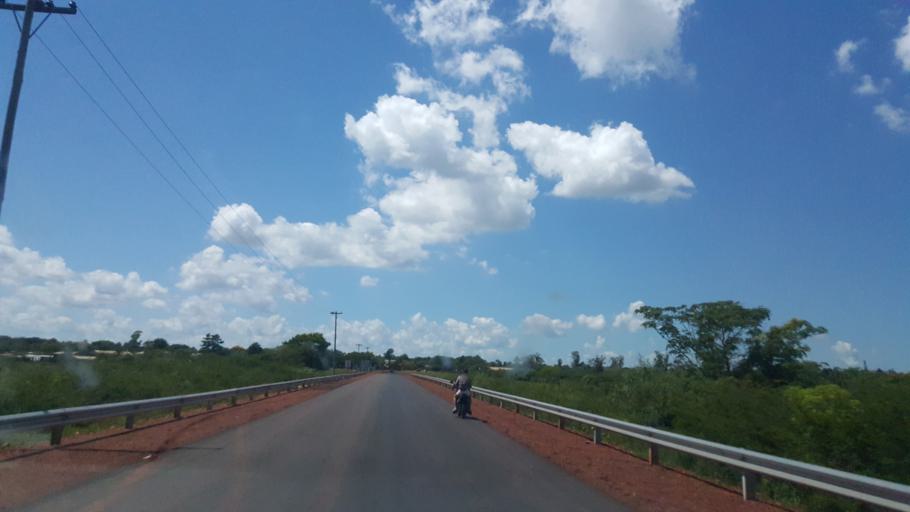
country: AR
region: Corrientes
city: Santo Tome
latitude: -28.5391
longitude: -56.0505
